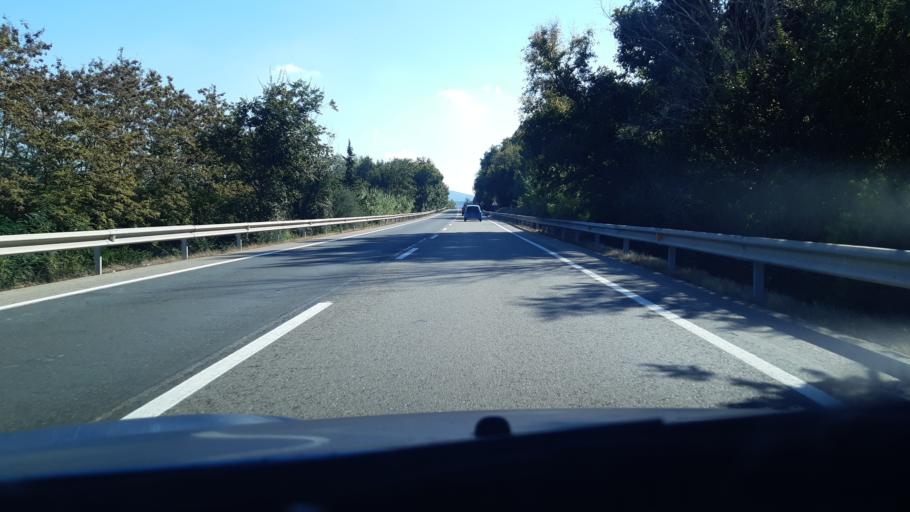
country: ES
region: Catalonia
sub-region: Provincia de Tarragona
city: Tivenys
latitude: 40.8647
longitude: 0.5061
